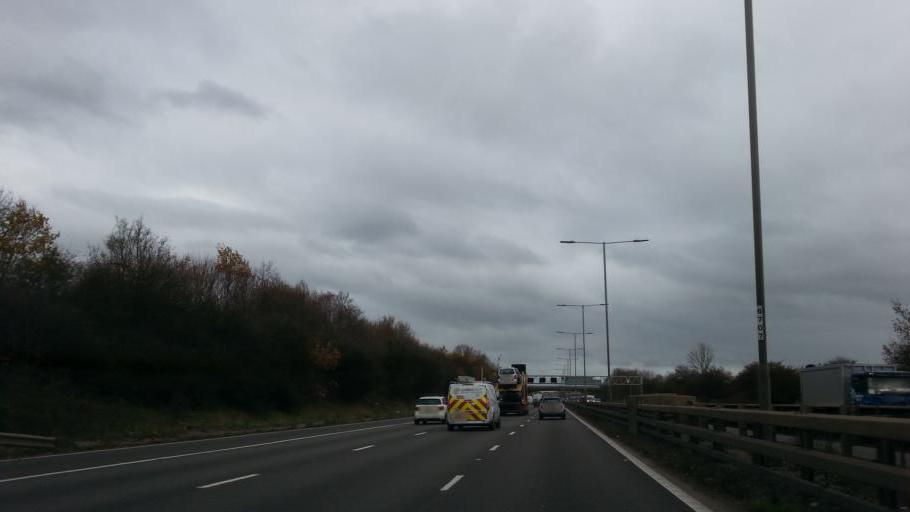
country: GB
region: England
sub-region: Solihull
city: Chelmsley Wood
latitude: 52.4951
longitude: -1.7355
